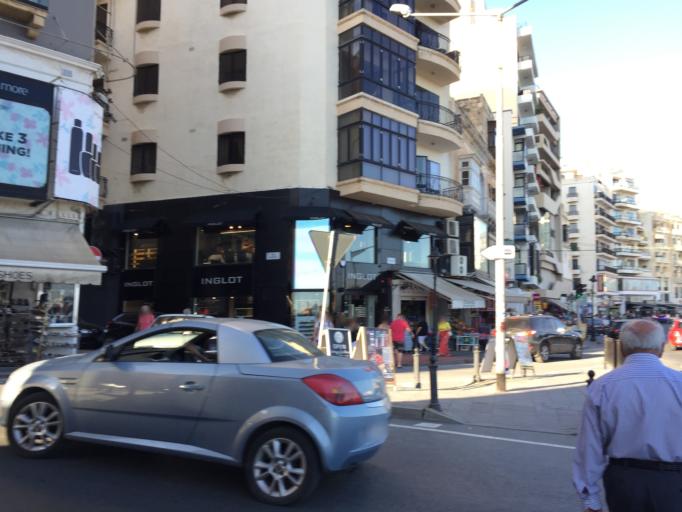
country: MT
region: Tas-Sliema
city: Sliema
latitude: 35.9091
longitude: 14.5034
